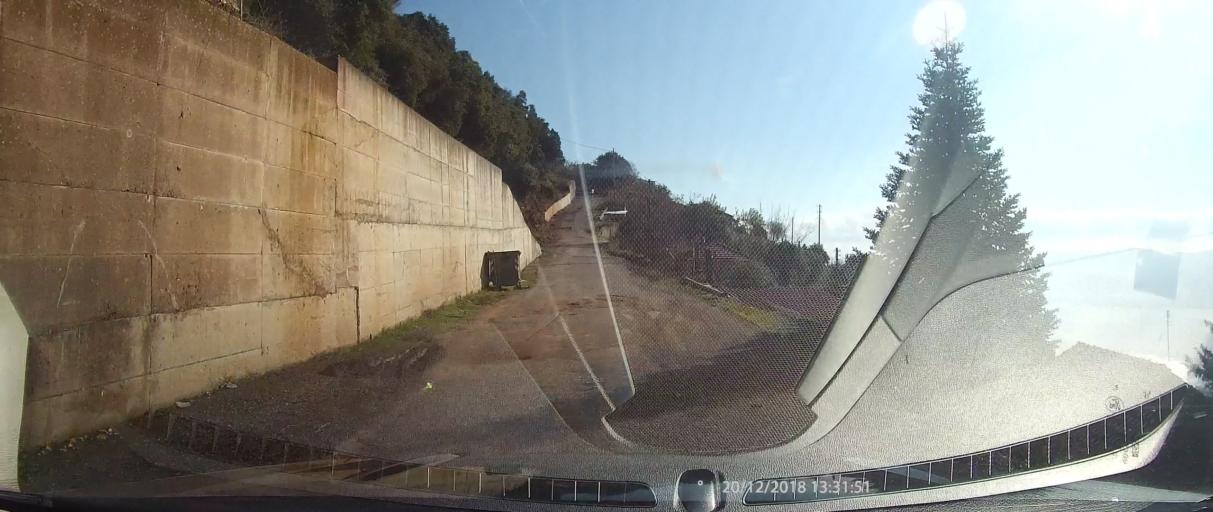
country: GR
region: West Greece
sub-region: Nomos Aitolias kai Akarnanias
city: Paravola
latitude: 38.6318
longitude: 21.5860
